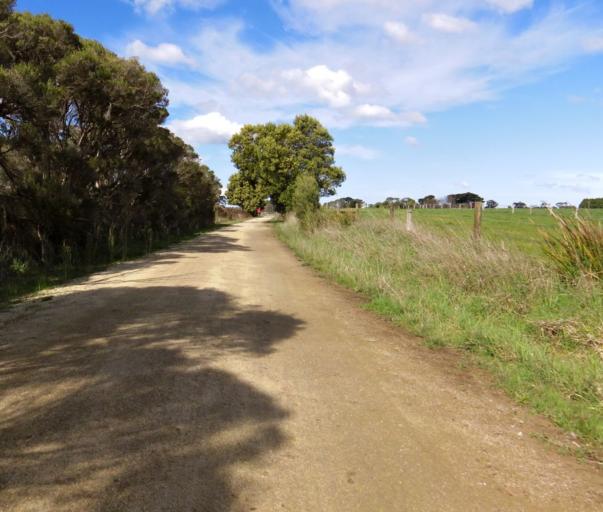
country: AU
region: Victoria
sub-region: Bass Coast
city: North Wonthaggi
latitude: -38.5167
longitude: 145.9429
